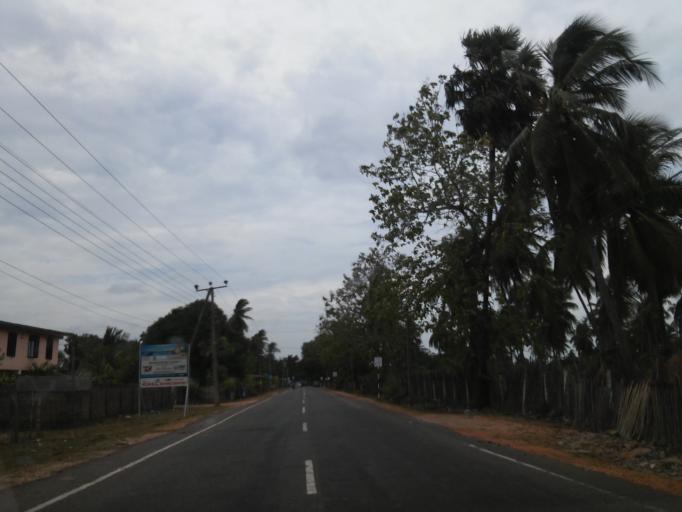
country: LK
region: Eastern Province
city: Trincomalee
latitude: 8.6860
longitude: 81.1883
